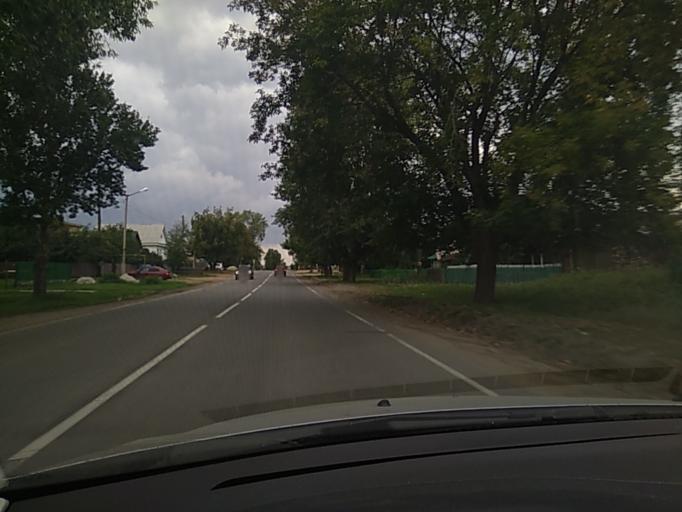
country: RU
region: Chelyabinsk
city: Kyshtym
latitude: 55.7077
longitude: 60.5188
